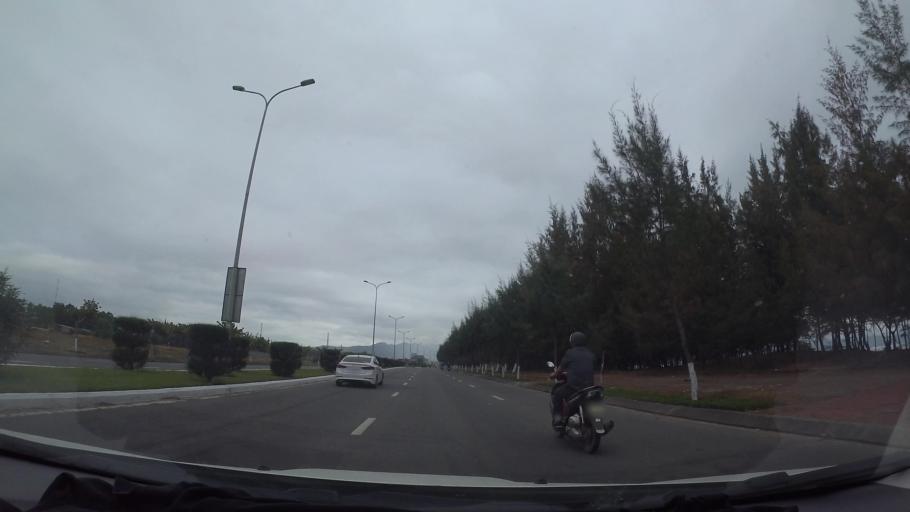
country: VN
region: Da Nang
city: Lien Chieu
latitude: 16.0970
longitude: 108.1441
